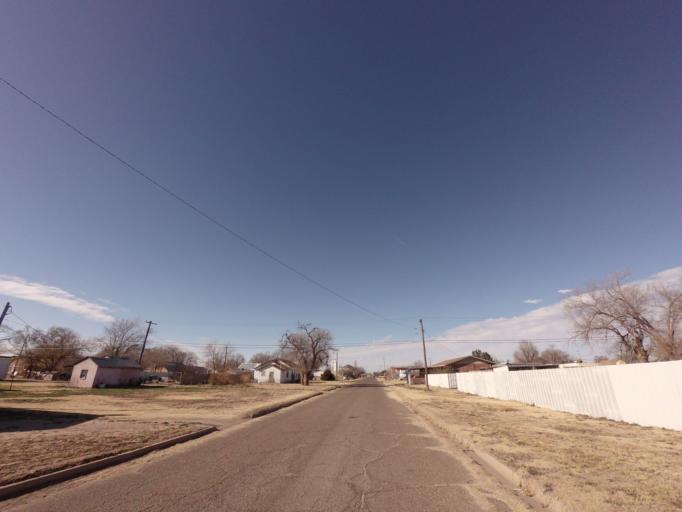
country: US
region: New Mexico
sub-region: Curry County
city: Clovis
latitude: 34.3997
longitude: -103.2132
